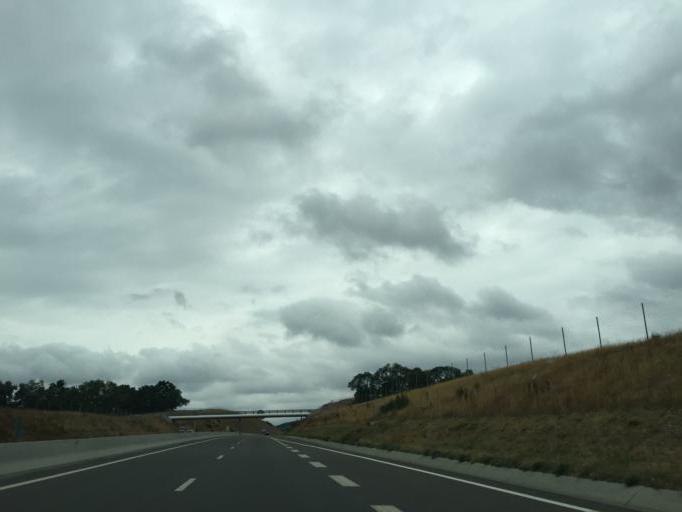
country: FR
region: Rhone-Alpes
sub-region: Departement de la Loire
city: Saint-Just-la-Pendue
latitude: 45.8524
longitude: 4.2249
